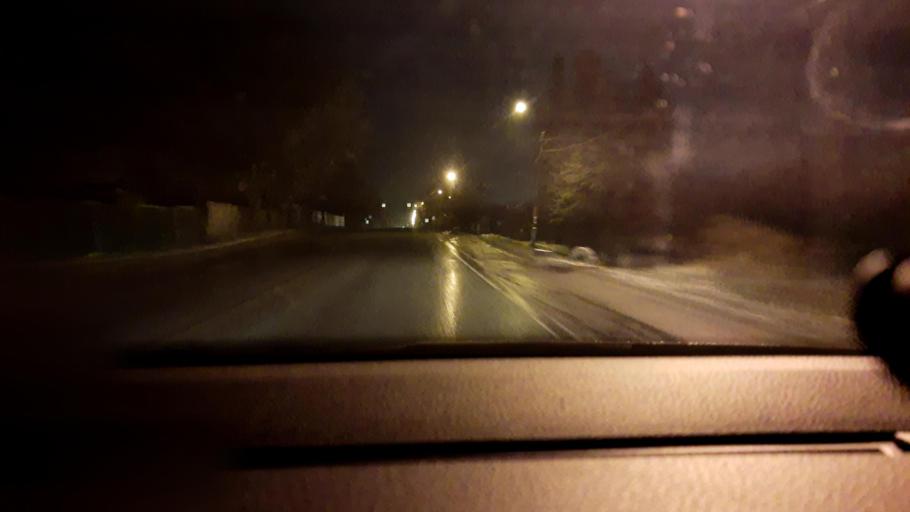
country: RU
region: Moskovskaya
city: Zagoryanskiy
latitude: 55.9412
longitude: 37.9633
